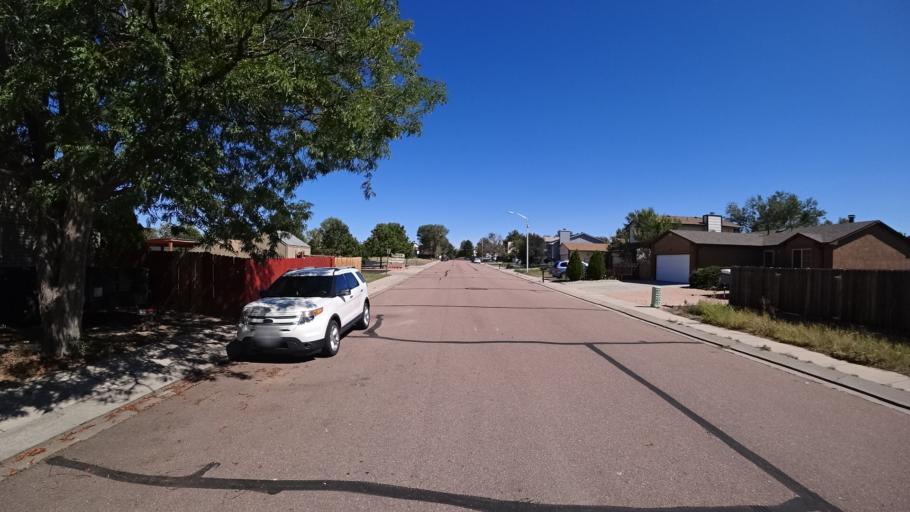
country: US
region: Colorado
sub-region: El Paso County
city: Stratmoor
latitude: 38.7878
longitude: -104.7468
